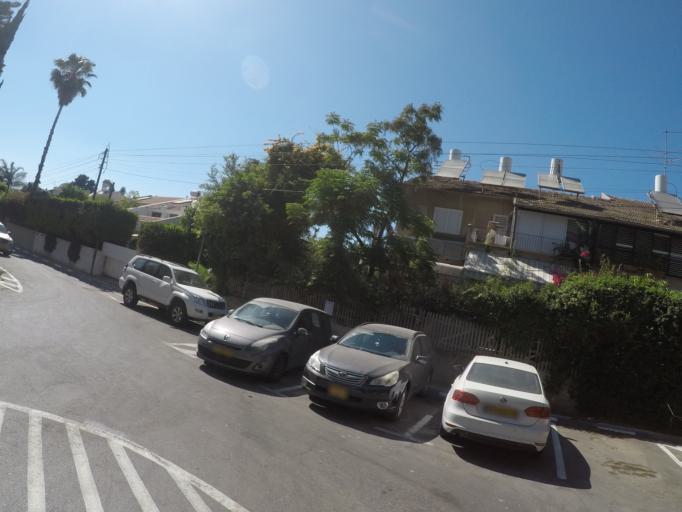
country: IL
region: Tel Aviv
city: Ramat Gan
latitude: 32.1087
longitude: 34.8004
